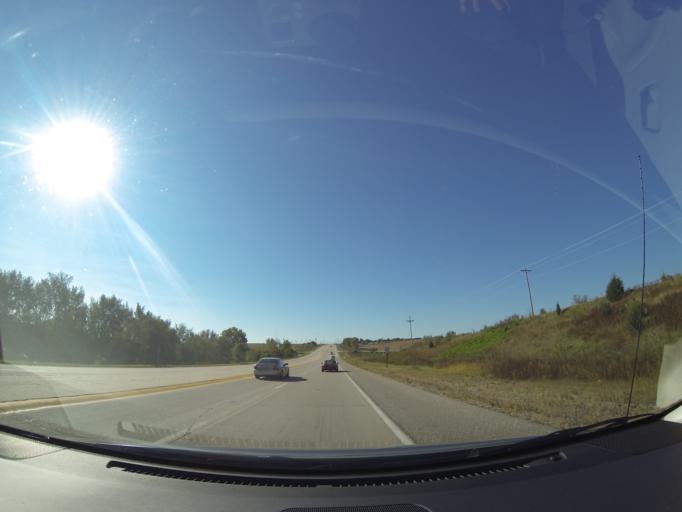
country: US
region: Nebraska
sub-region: Sarpy County
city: Gretna
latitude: 41.1062
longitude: -96.2534
